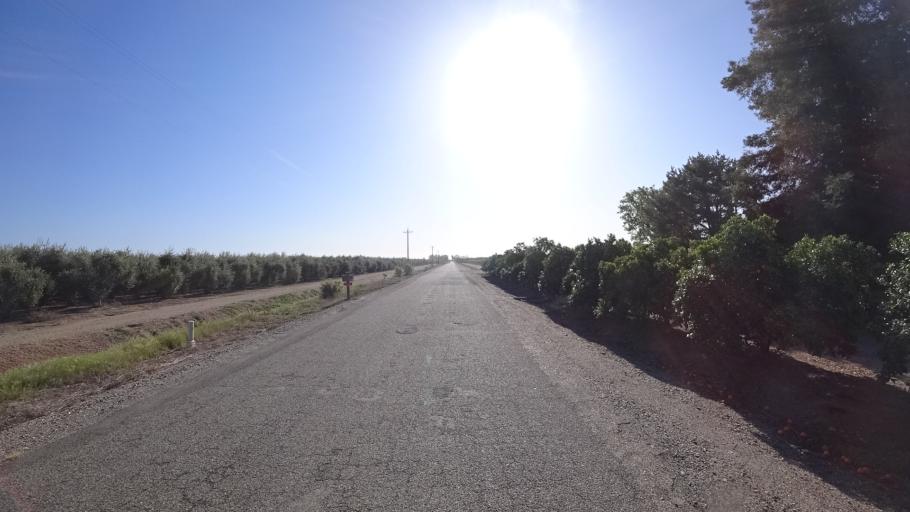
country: US
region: California
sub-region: Glenn County
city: Orland
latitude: 39.6815
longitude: -122.1358
